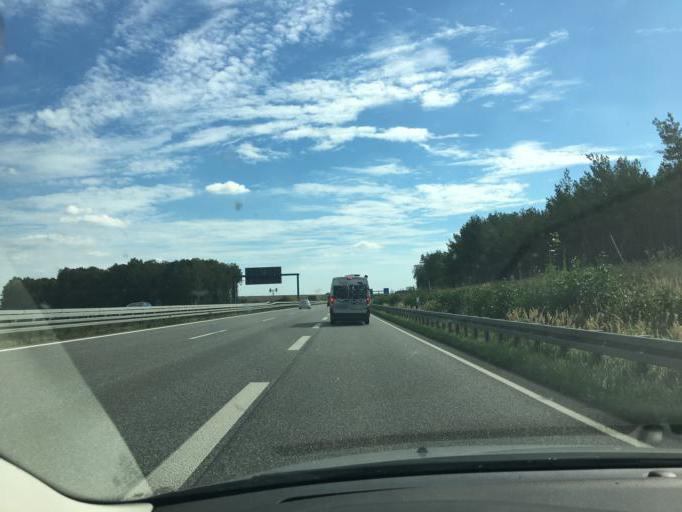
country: DE
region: Mecklenburg-Vorpommern
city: Mirow
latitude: 53.4267
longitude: 11.5113
